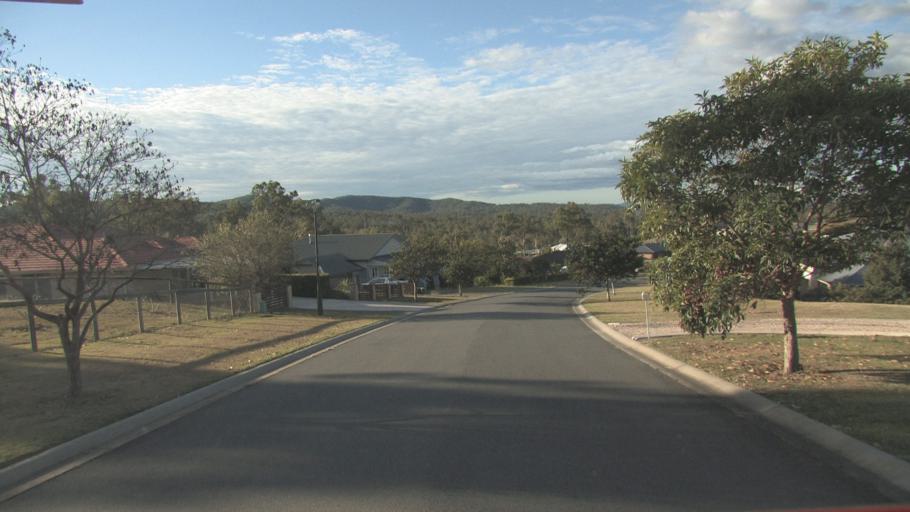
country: AU
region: Queensland
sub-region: Logan
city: Cedar Vale
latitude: -27.8678
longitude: 153.0804
